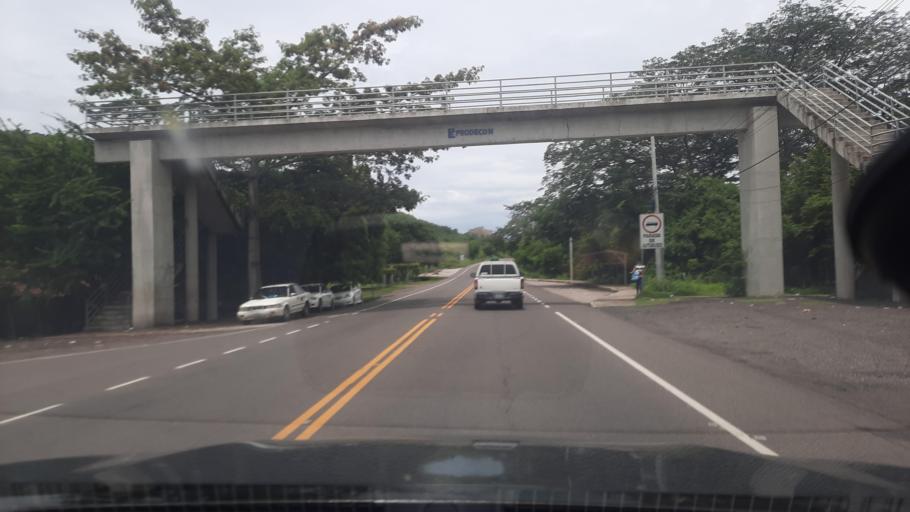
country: HN
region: Valle
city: Langue
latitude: 13.5904
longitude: -87.6957
